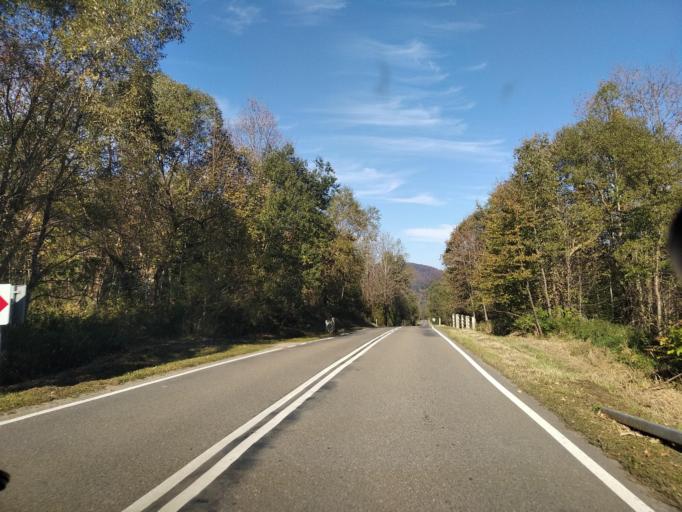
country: PL
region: Subcarpathian Voivodeship
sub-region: Powiat leski
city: Cisna
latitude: 49.2537
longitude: 22.2849
